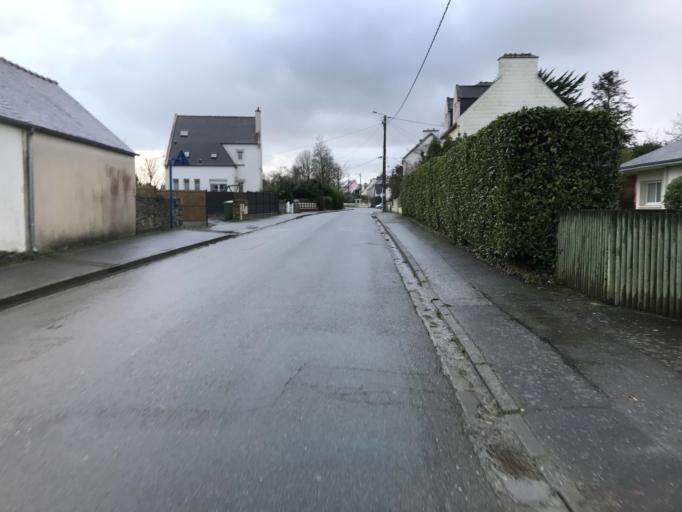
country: FR
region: Brittany
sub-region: Departement du Finistere
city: Loperhet
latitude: 48.3768
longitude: -4.3131
